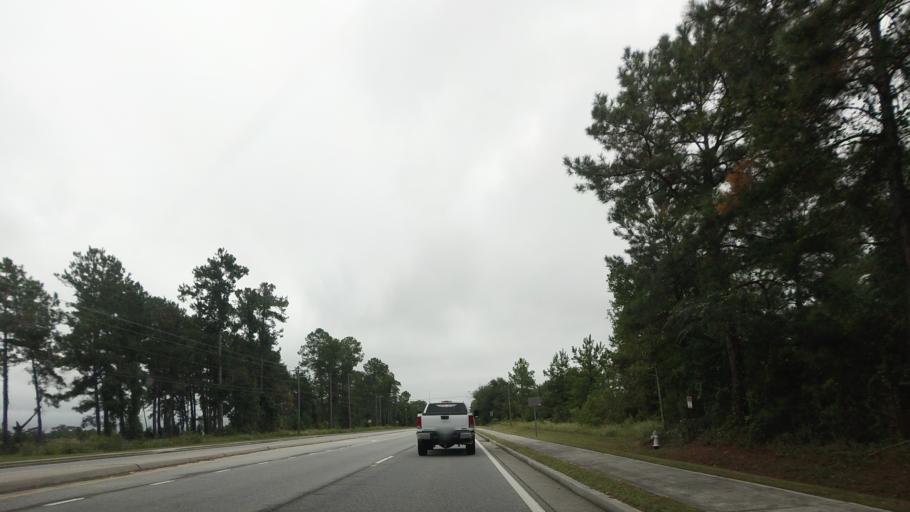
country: US
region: Georgia
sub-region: Berrien County
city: Ray City
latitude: 30.9512
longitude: -83.2289
